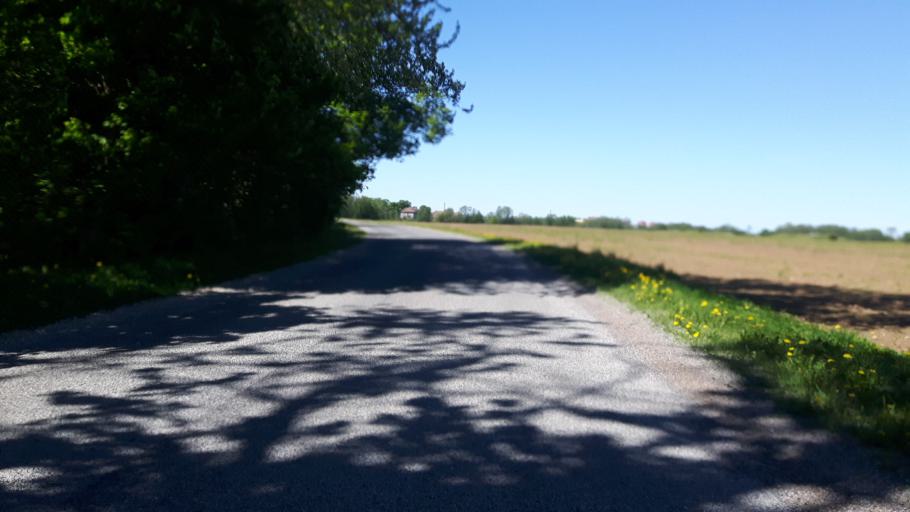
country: EE
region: Ida-Virumaa
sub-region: Sillamaee linn
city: Sillamae
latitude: 59.3818
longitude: 27.8248
